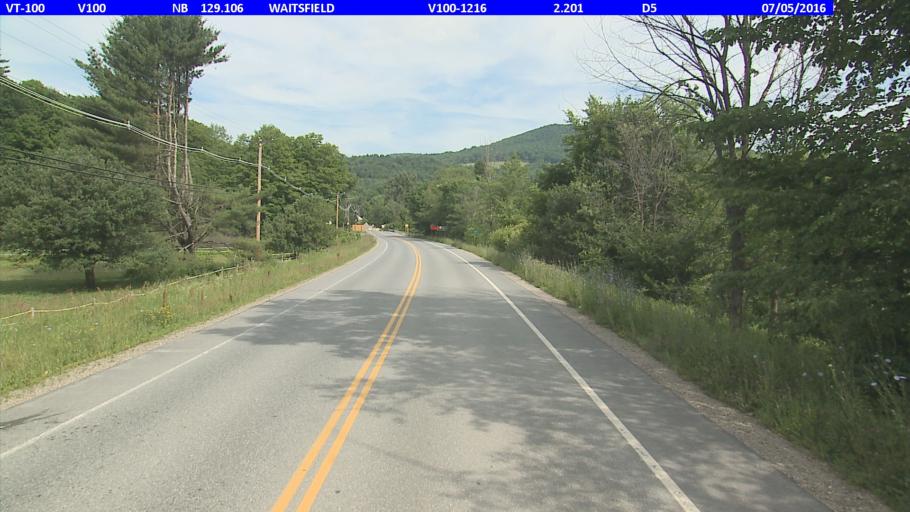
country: US
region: Vermont
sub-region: Washington County
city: Waterbury
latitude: 44.1768
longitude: -72.8345
